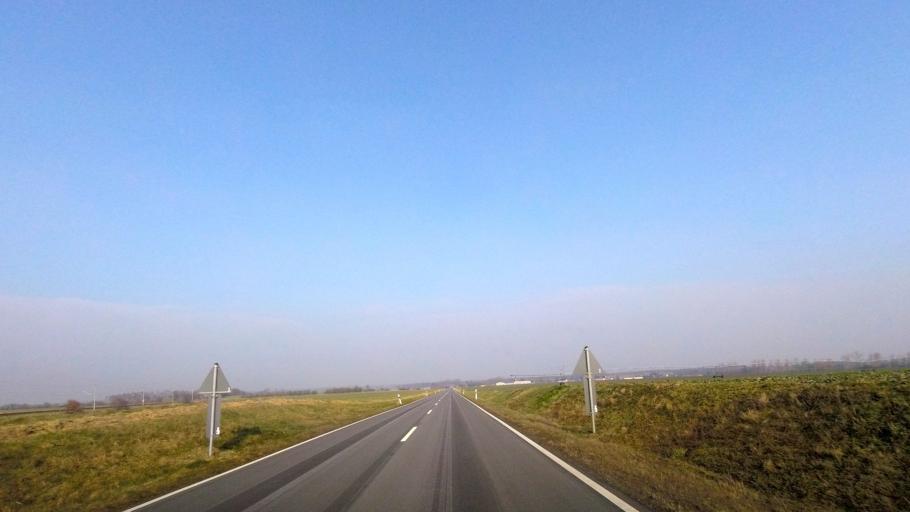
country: DE
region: Brandenburg
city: Juterbog
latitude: 51.9520
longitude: 13.0401
